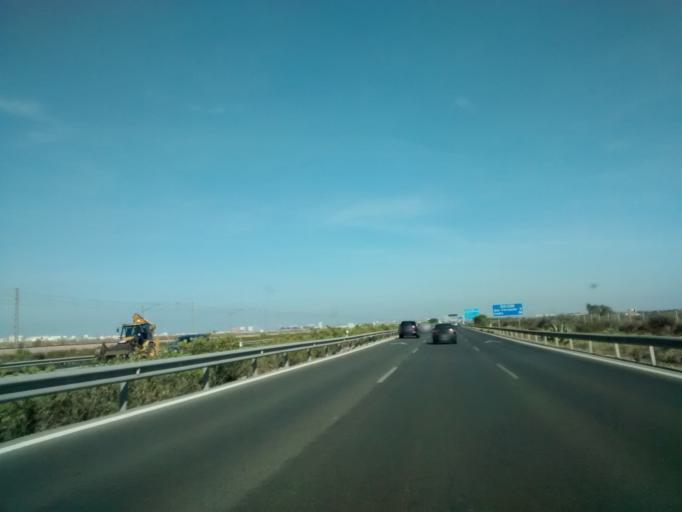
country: ES
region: Andalusia
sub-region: Provincia de Cadiz
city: Chiclana de la Frontera
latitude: 36.4575
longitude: -6.1570
